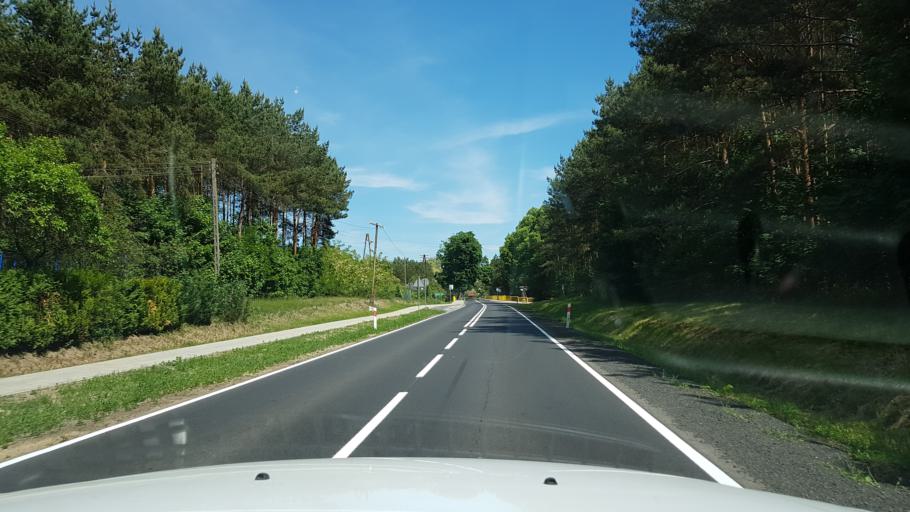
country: PL
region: West Pomeranian Voivodeship
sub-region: Powiat gryfinski
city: Chojna
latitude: 52.9606
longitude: 14.4755
